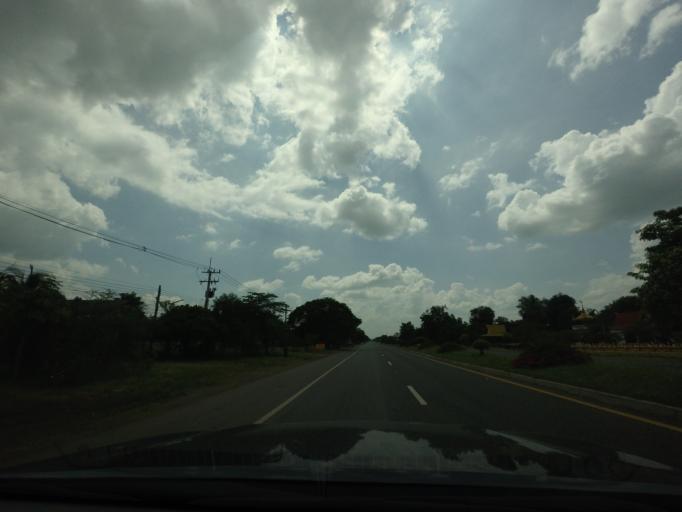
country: TH
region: Phetchabun
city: Nong Phai
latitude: 16.1762
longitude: 101.0822
